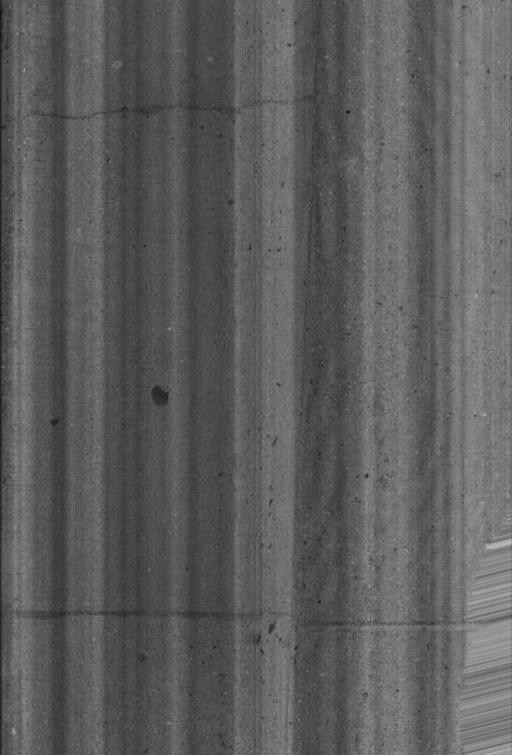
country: US
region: Maryland
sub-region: Prince George's County
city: Glassmanor
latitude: 38.8637
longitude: -77.0014
